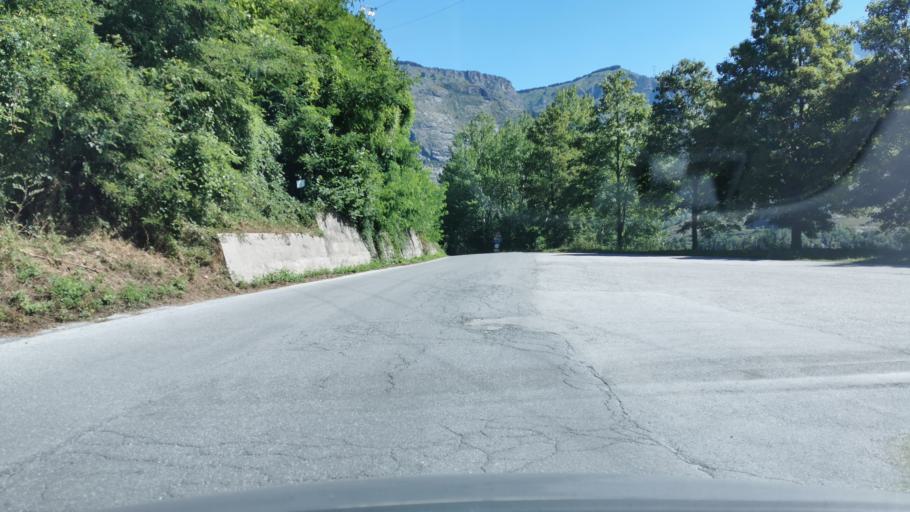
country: IT
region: Piedmont
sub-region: Provincia di Cuneo
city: Entracque
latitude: 44.2328
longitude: 7.3913
